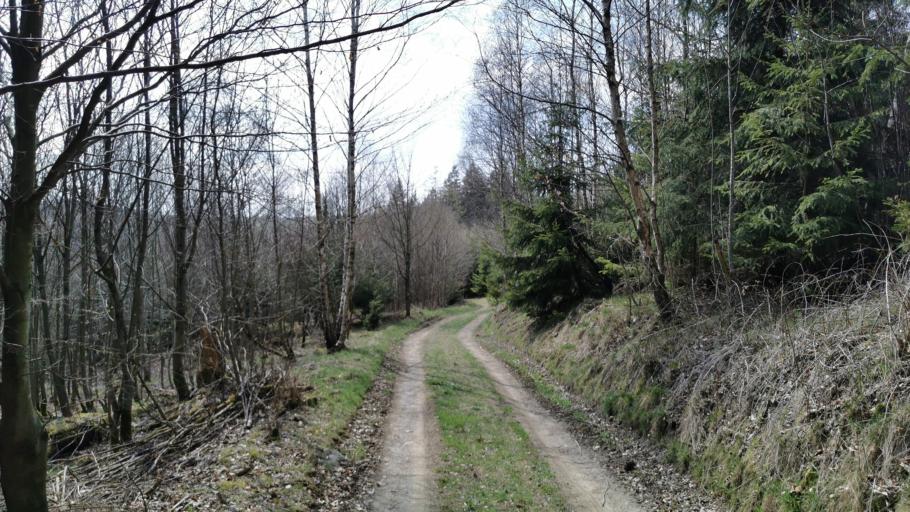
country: DE
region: Bavaria
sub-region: Upper Franconia
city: Ludwigsstadt
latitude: 50.4721
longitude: 11.4272
